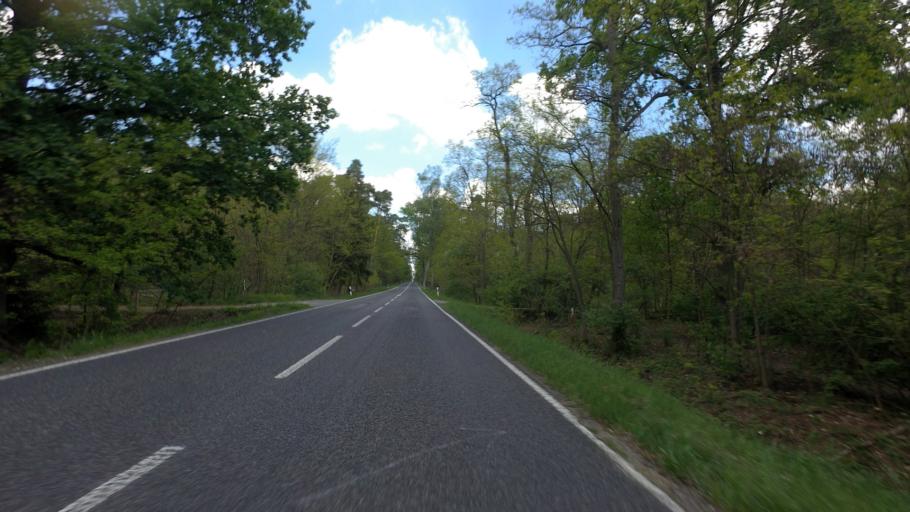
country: DE
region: Brandenburg
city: Straupitz
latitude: 51.9532
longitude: 14.1795
